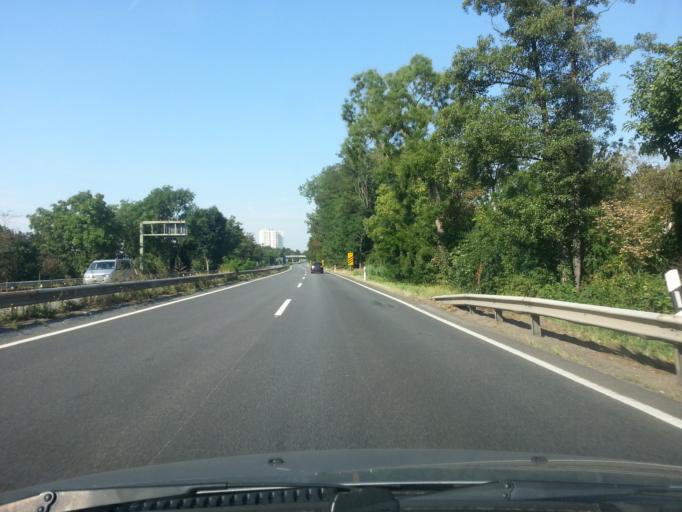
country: DE
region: Rheinland-Pfalz
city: Frankenthal
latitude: 49.5358
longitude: 8.3765
